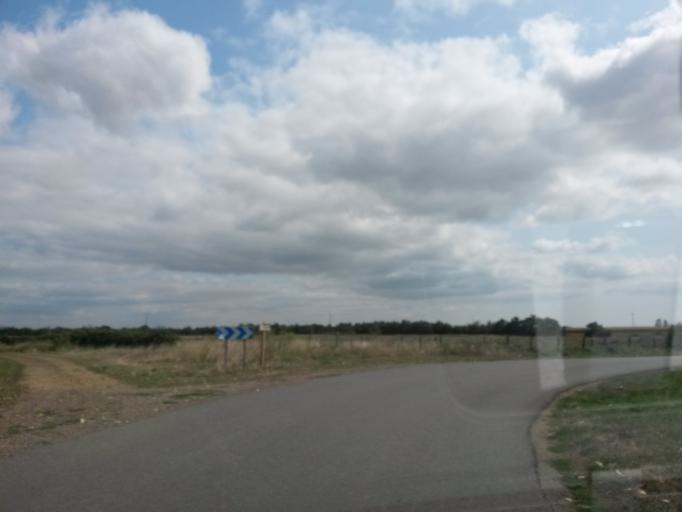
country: FR
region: Pays de la Loire
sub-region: Departement de la Vendee
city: Saint-Hilaire-de-Talmont
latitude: 46.4410
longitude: -1.6023
